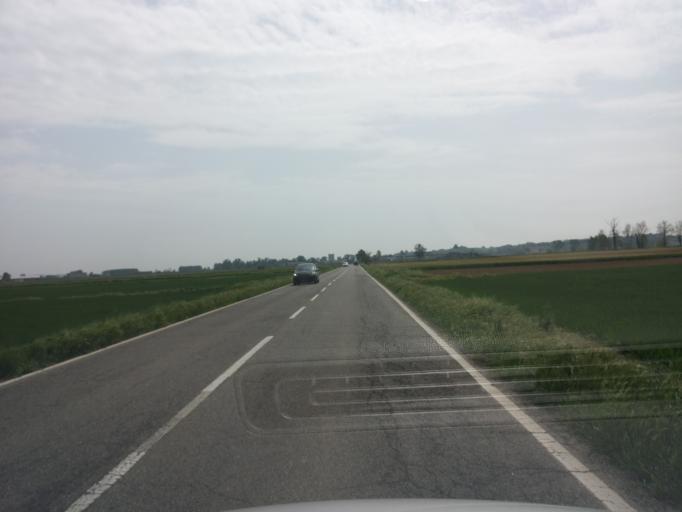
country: IT
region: Piedmont
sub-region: Provincia di Alessandria
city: Terruggia
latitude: 45.0836
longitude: 8.4732
